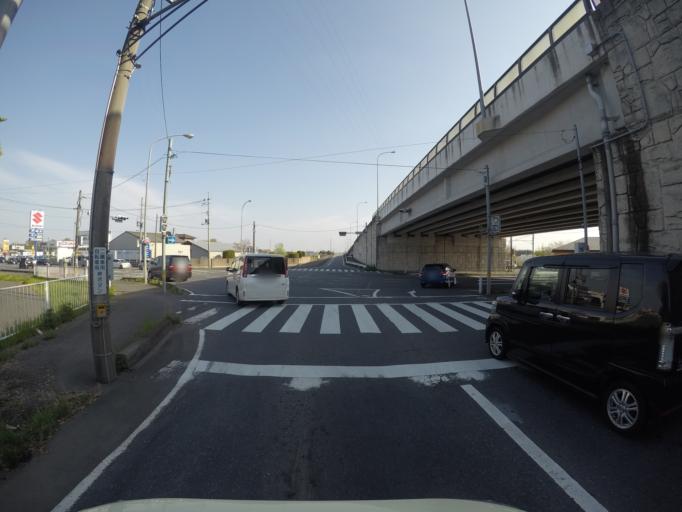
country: JP
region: Ibaraki
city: Ishige
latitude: 36.1881
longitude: 139.9886
